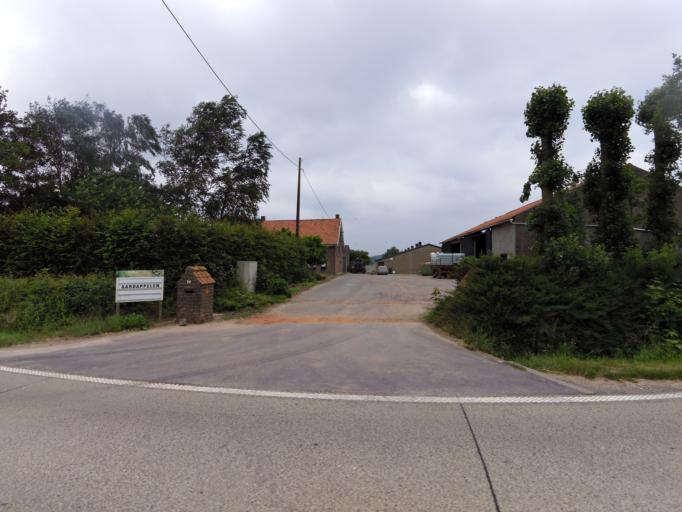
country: FR
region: Nord-Pas-de-Calais
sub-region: Departement du Nord
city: Saint-Jans-Cappel
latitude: 50.7738
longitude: 2.7760
